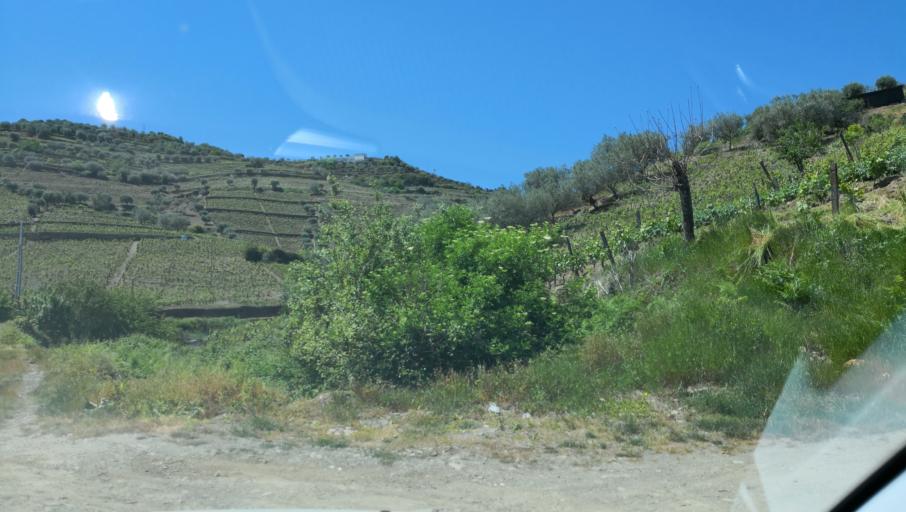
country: PT
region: Vila Real
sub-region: Vila Real
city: Vila Real
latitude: 41.2279
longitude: -7.7210
